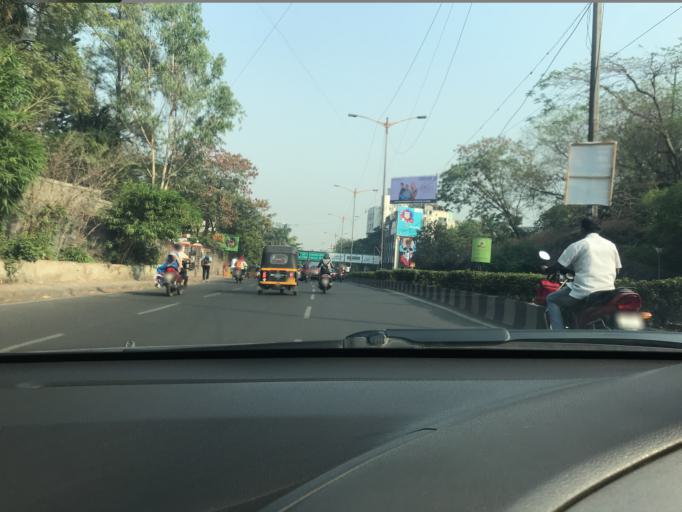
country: IN
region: Maharashtra
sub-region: Pune Division
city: Shivaji Nagar
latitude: 18.5233
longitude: 73.8295
